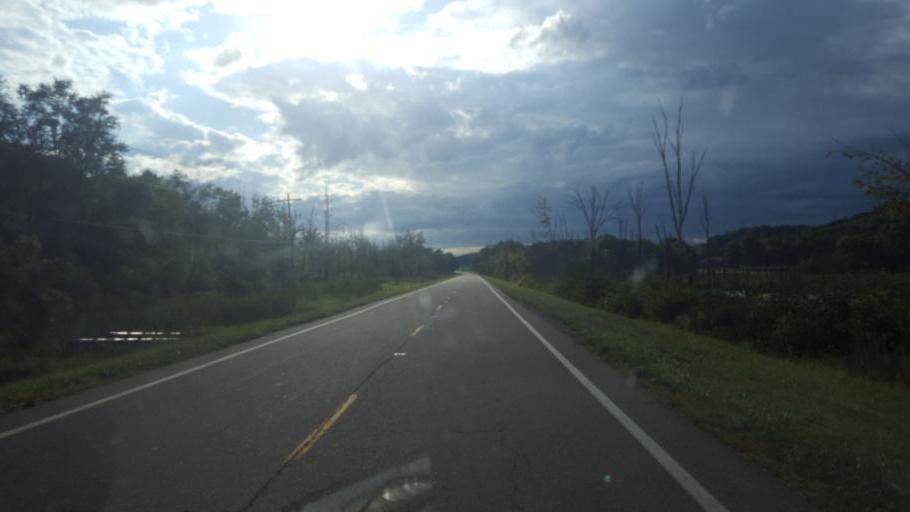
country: US
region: Ohio
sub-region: Holmes County
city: Millersburg
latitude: 40.4815
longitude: -81.9952
